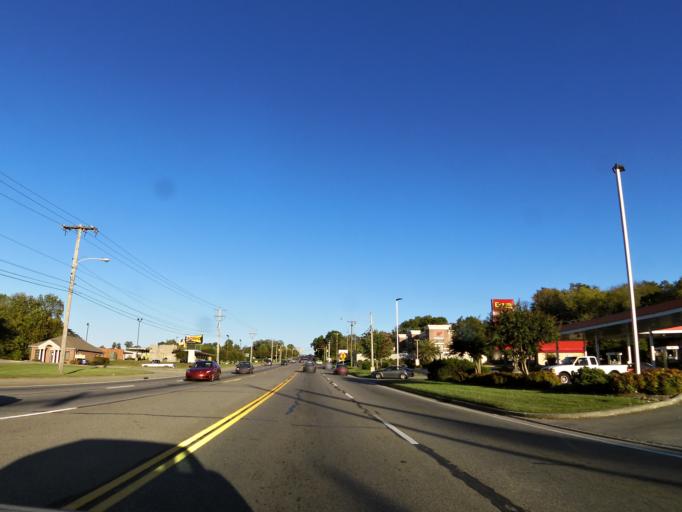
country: US
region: Tennessee
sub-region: Blount County
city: Maryville
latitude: 35.7551
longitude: -83.9521
